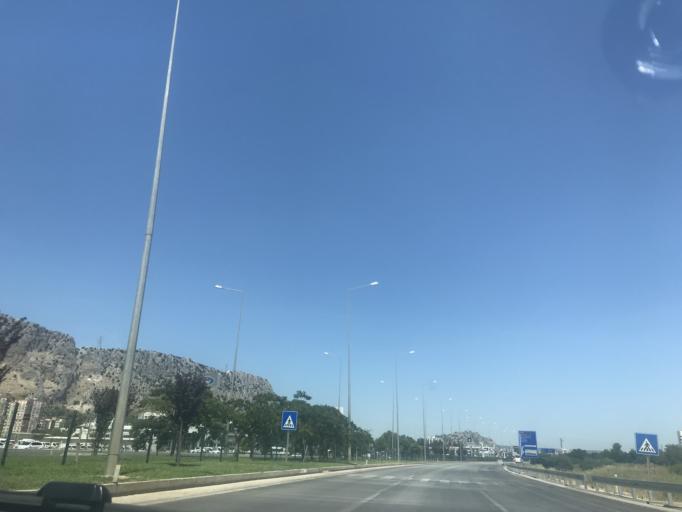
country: TR
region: Antalya
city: Cakirlar
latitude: 36.8380
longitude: 30.5960
